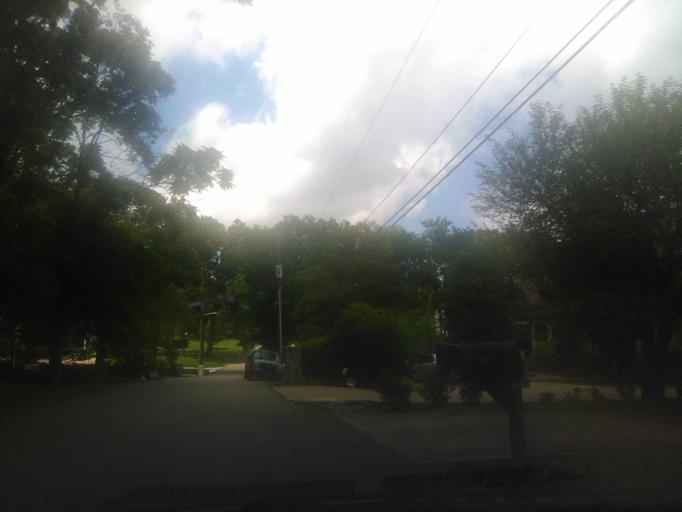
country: US
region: Tennessee
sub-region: Davidson County
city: Belle Meade
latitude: 36.1052
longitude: -86.8361
